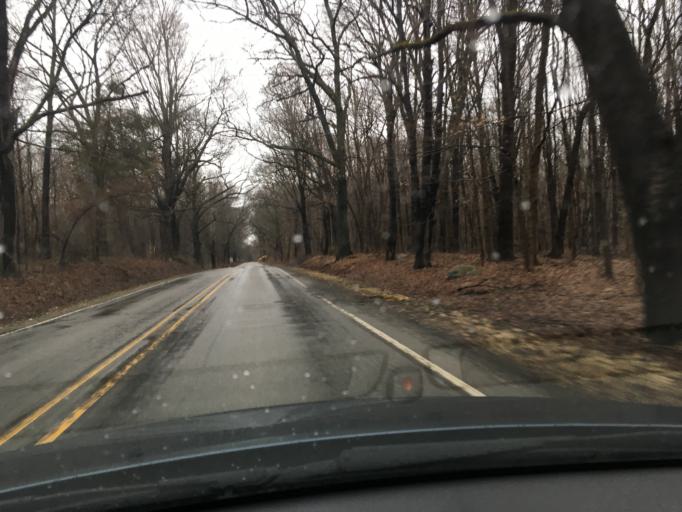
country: US
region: Michigan
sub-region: Jackson County
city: Grass Lake
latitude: 42.3248
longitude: -84.1557
